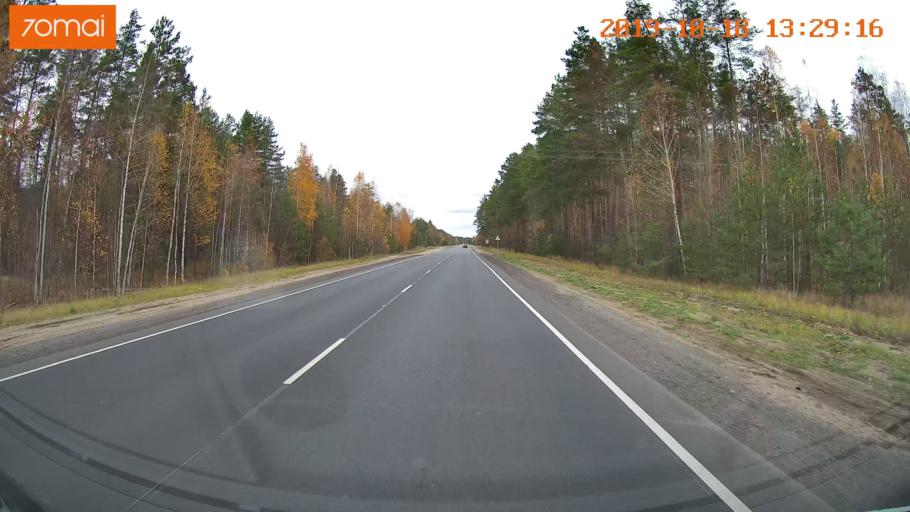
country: RU
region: Rjazan
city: Solotcha
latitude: 54.7919
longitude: 39.8738
